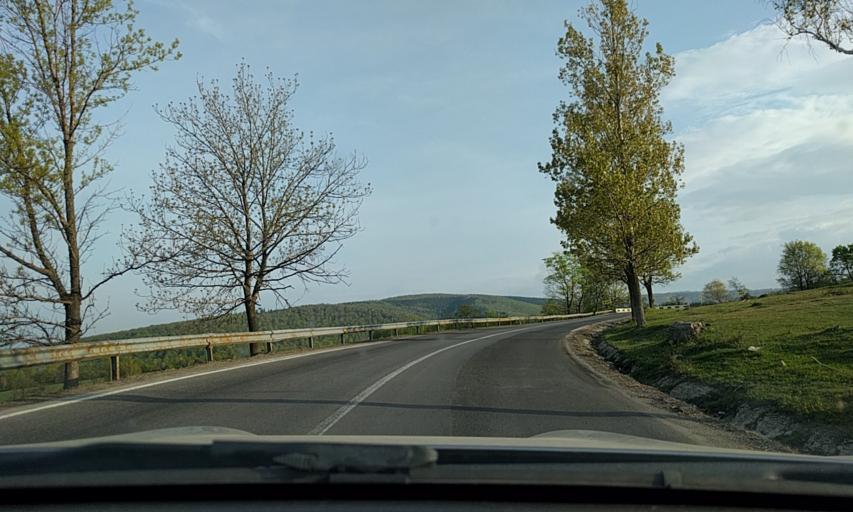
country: RO
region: Covasna
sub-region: Comuna Bretcu
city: Bretcu
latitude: 46.0443
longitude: 26.3345
